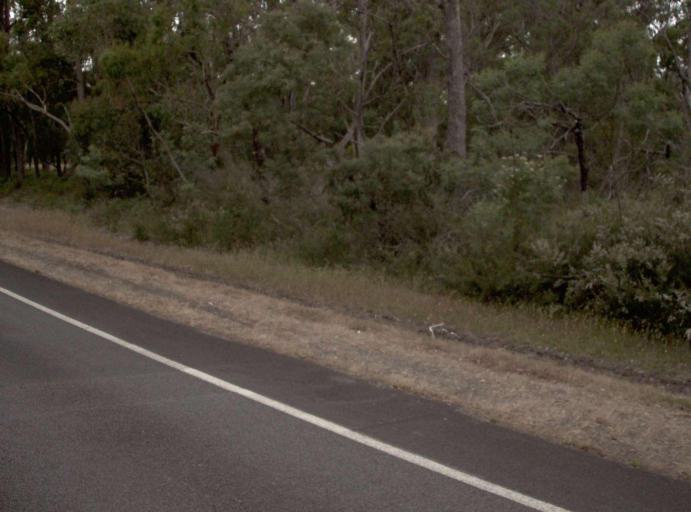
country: AU
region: Victoria
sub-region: Wellington
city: Sale
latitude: -38.5055
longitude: 146.8935
